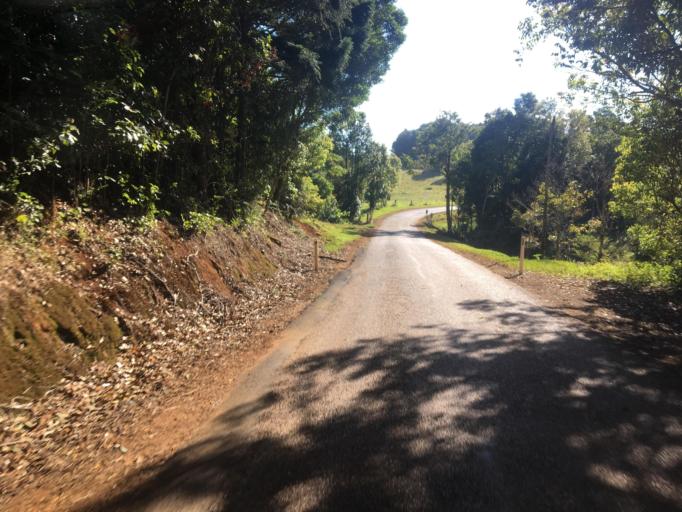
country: AU
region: Queensland
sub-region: Tablelands
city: Ravenshoe
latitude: -17.6025
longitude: 145.5641
